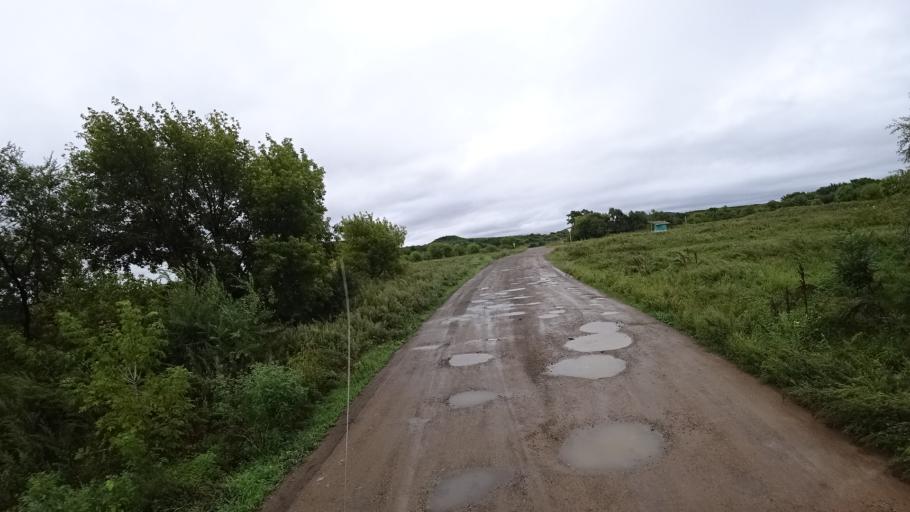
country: RU
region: Primorskiy
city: Monastyrishche
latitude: 44.2769
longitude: 132.4232
